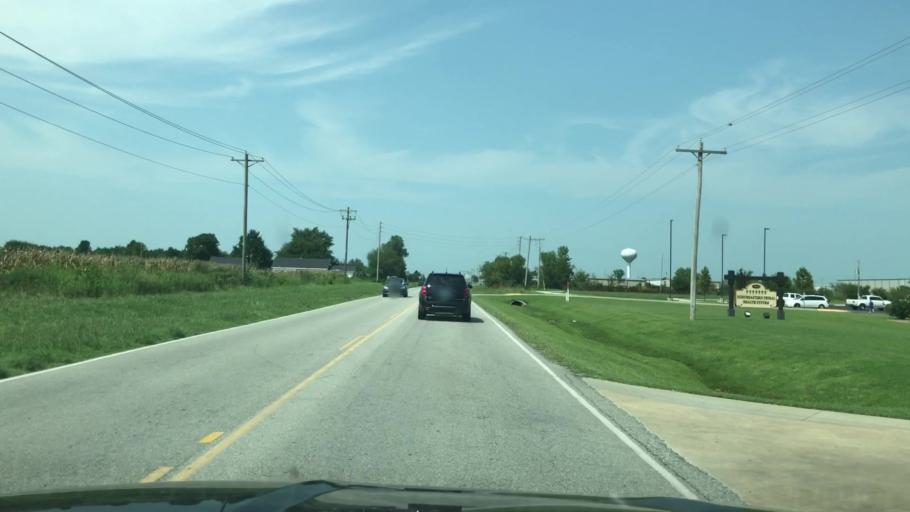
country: US
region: Oklahoma
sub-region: Ottawa County
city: Commerce
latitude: 36.9057
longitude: -94.8419
